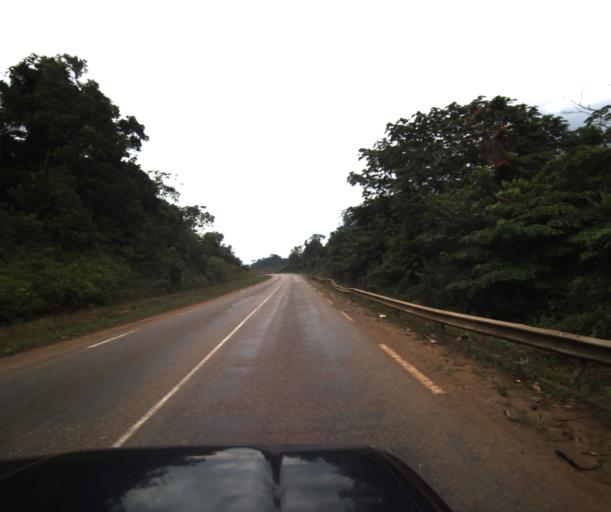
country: CM
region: Littoral
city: Edea
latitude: 3.8607
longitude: 10.0790
